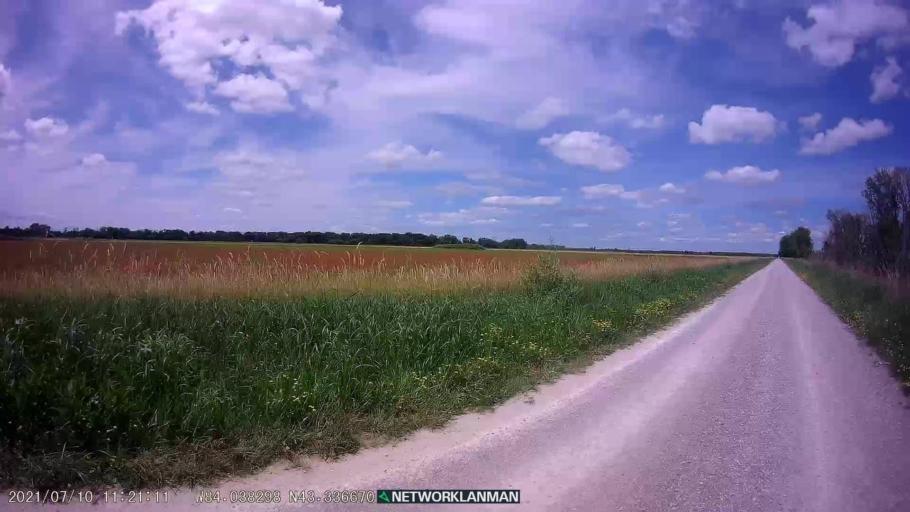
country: US
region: Michigan
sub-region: Saginaw County
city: Shields
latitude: 43.3368
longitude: -84.0386
